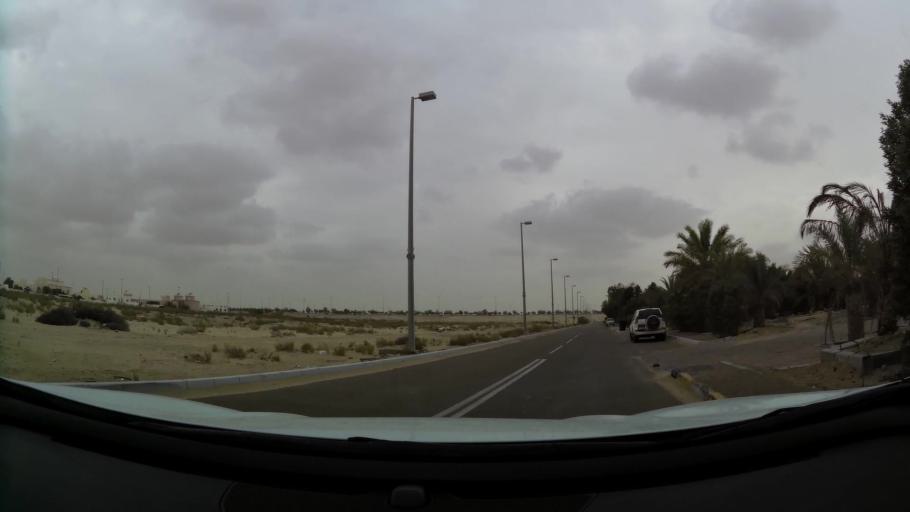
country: AE
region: Abu Dhabi
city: Abu Dhabi
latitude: 24.3886
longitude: 54.6555
